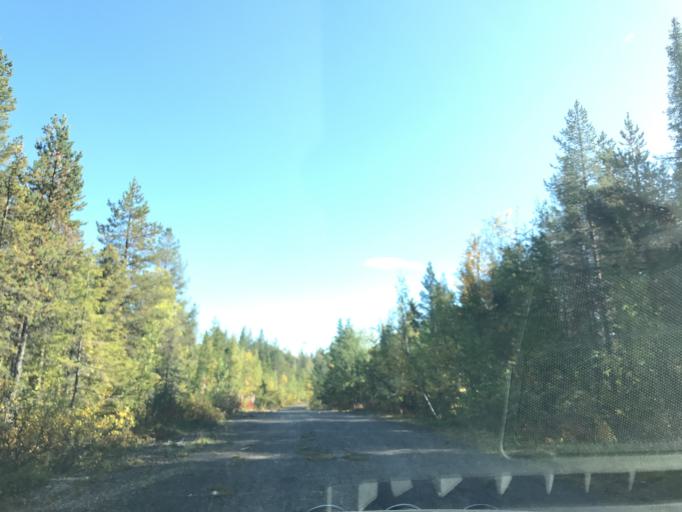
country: SE
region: Norrbotten
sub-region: Gallivare Kommun
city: Malmberget
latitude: 67.6469
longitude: 21.0965
